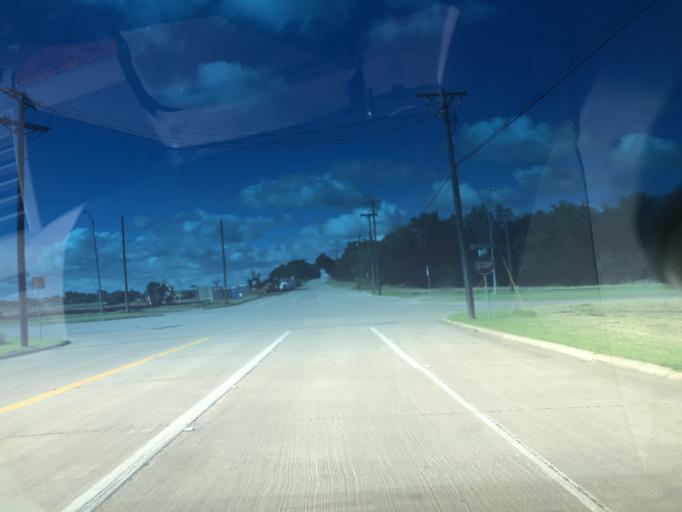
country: US
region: Texas
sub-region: Dallas County
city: Grand Prairie
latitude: 32.7998
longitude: -97.0204
